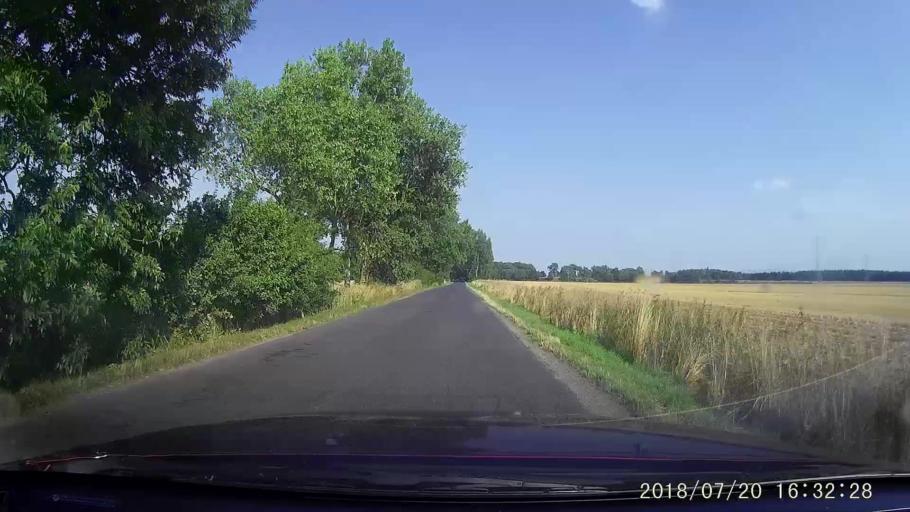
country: PL
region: Lower Silesian Voivodeship
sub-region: Powiat zgorzelecki
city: Sulikow
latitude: 51.0950
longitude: 15.0856
